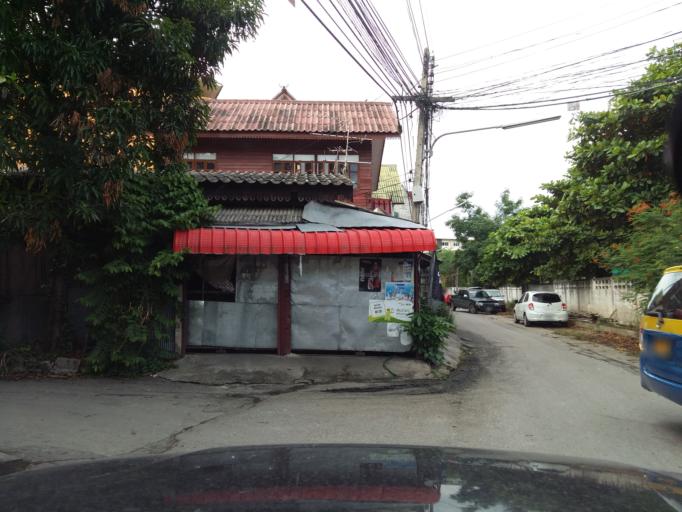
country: TH
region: Chiang Mai
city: Chiang Mai
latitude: 18.7826
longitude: 98.9952
